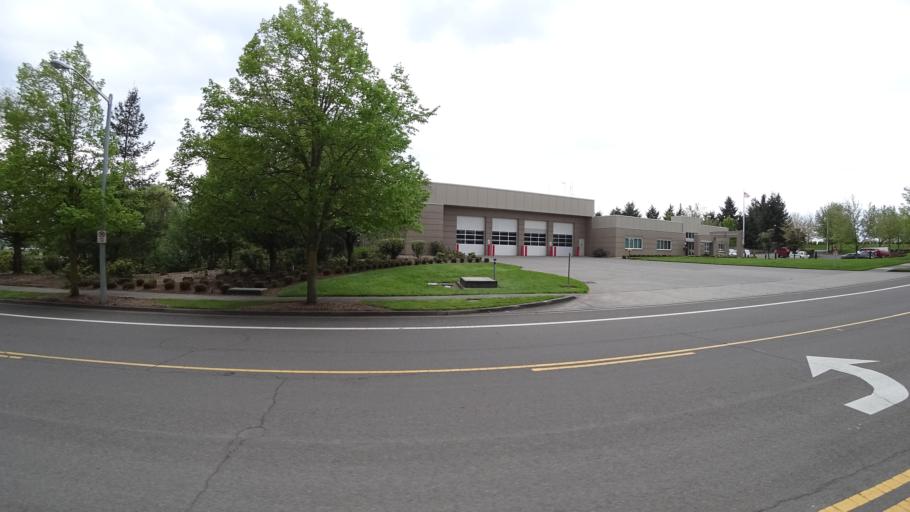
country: US
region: Oregon
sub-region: Washington County
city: Rockcreek
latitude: 45.5509
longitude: -122.9095
